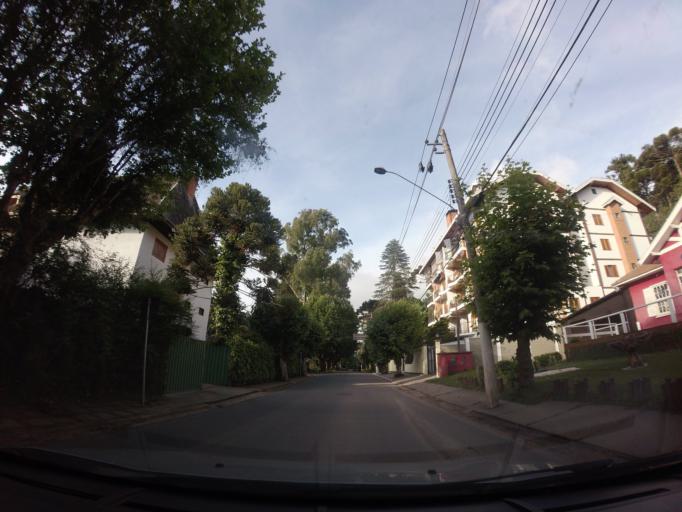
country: BR
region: Sao Paulo
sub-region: Campos Do Jordao
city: Campos do Jordao
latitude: -22.7269
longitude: -45.5687
